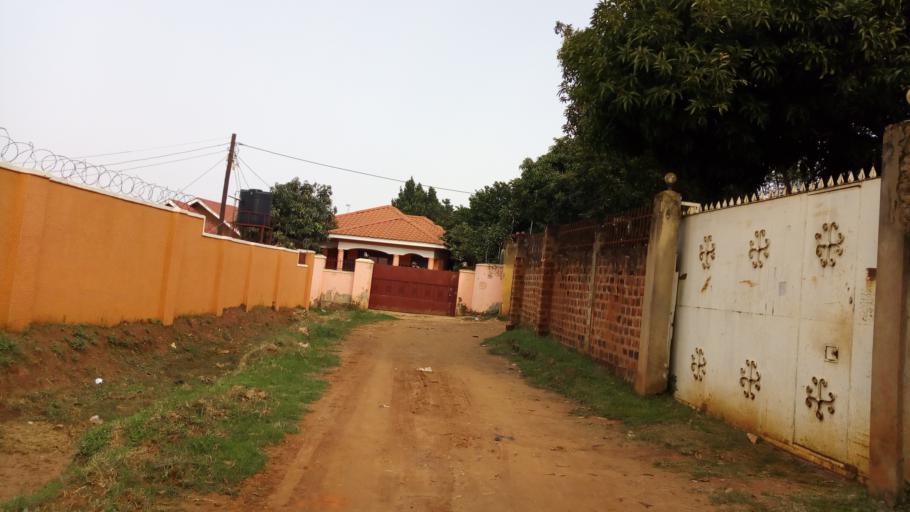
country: UG
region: Central Region
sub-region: Wakiso District
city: Kireka
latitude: 0.3144
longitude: 32.6483
